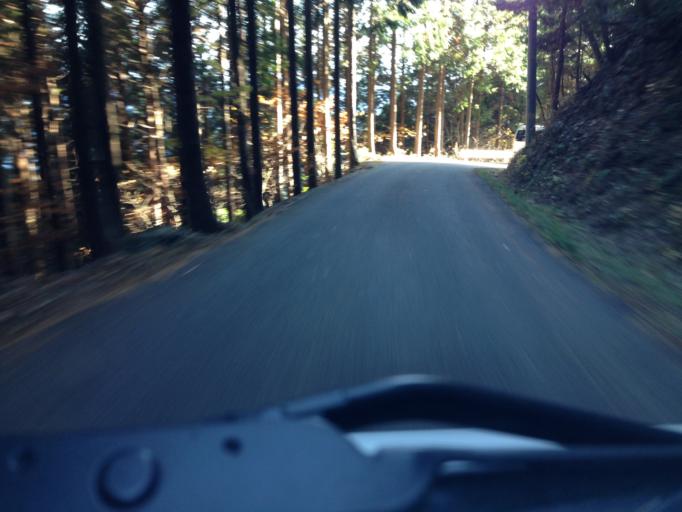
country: JP
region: Gifu
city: Mitake
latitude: 35.6170
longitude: 137.2232
